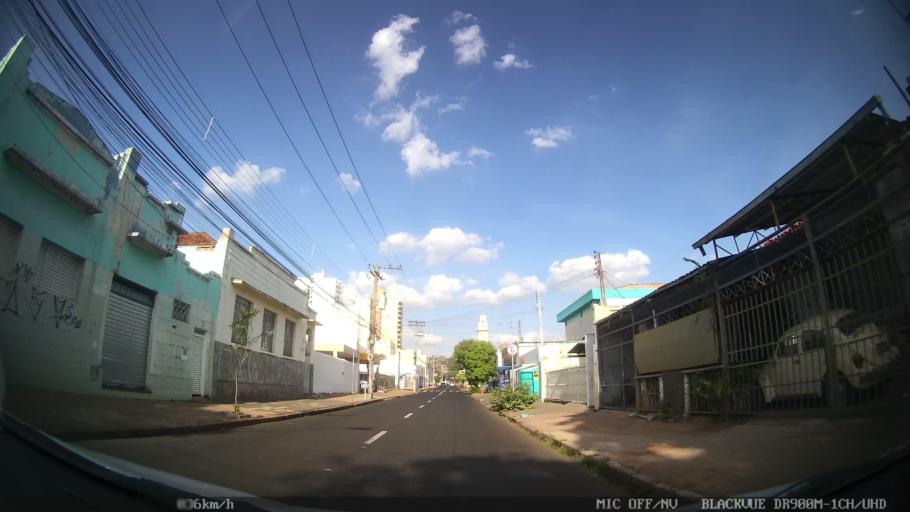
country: BR
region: Sao Paulo
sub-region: Ribeirao Preto
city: Ribeirao Preto
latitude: -21.1663
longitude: -47.8064
